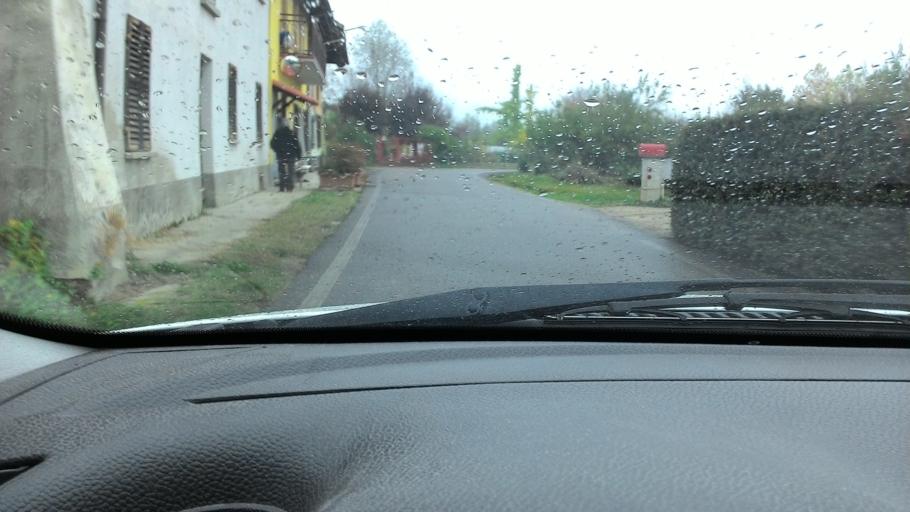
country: IT
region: Piedmont
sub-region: Provincia di Asti
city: Baldichieri d'Asti
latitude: 44.8976
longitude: 8.1255
